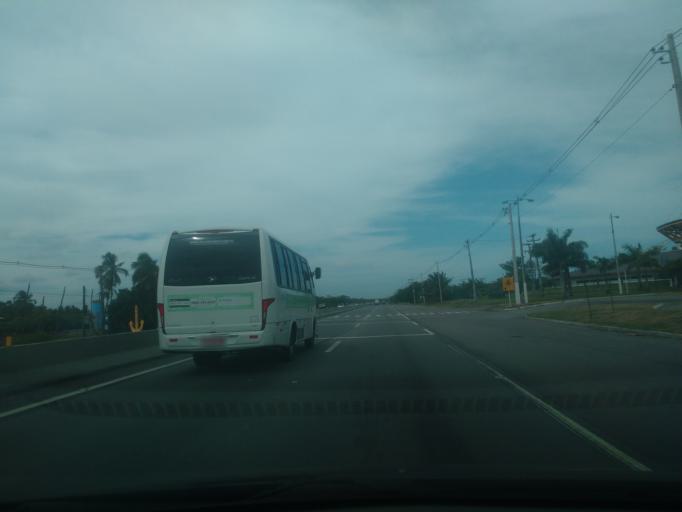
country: BR
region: Alagoas
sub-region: Maceio
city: Maceio
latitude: -9.7021
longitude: -35.8039
